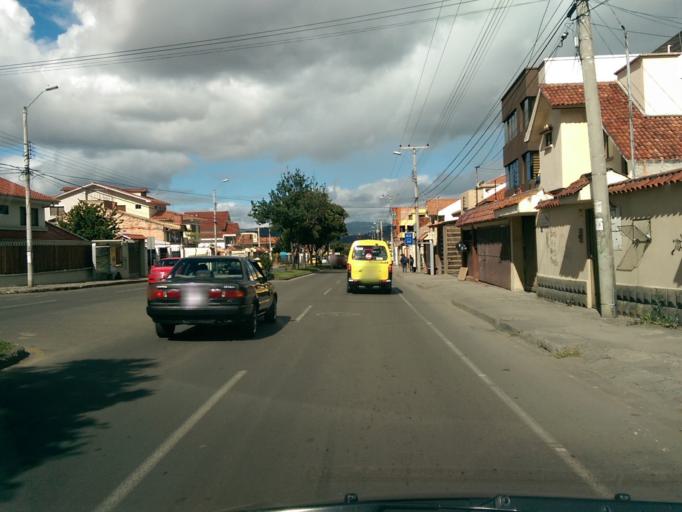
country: EC
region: Azuay
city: Cuenca
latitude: -2.9071
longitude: -79.0215
